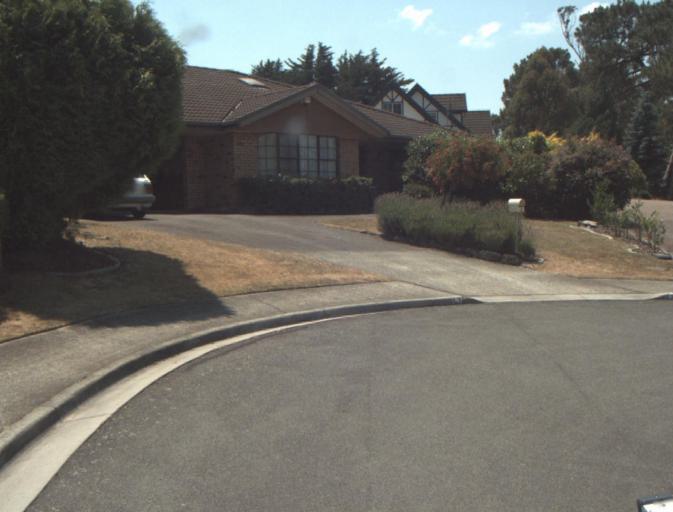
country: AU
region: Tasmania
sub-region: Launceston
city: Newstead
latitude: -41.4696
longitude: 147.1838
